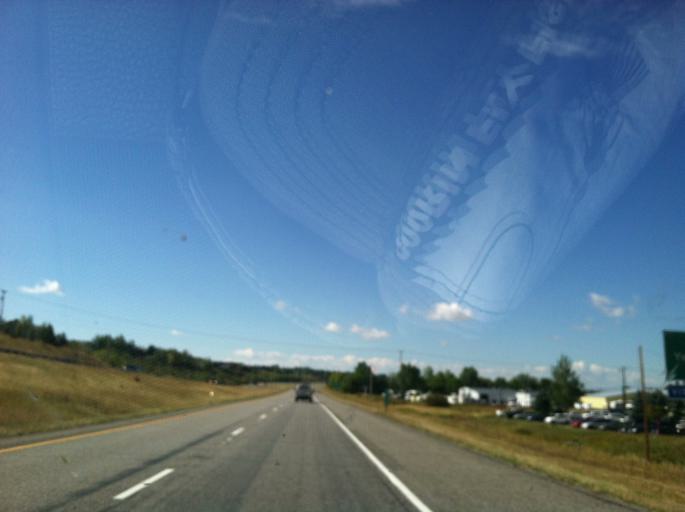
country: US
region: Montana
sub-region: Gallatin County
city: Bozeman
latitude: 45.6712
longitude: -110.9995
